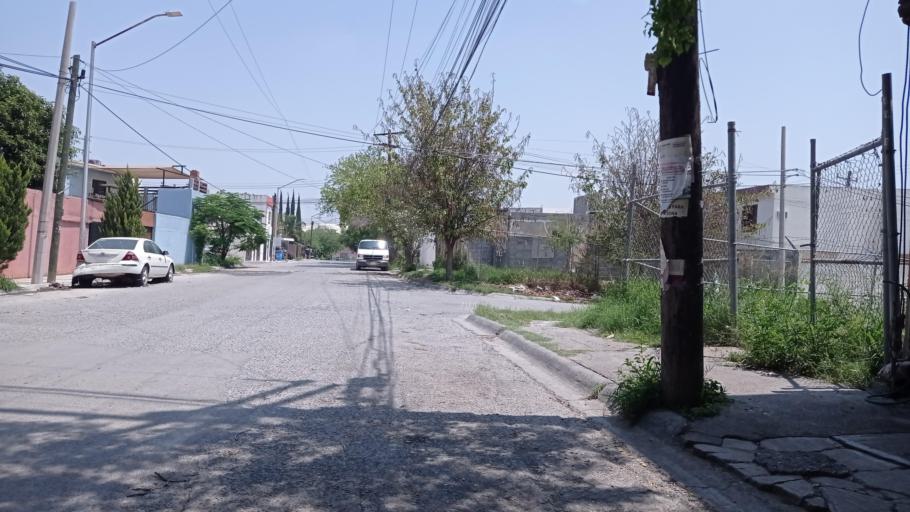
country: MX
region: Nuevo Leon
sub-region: Juarez
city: Jardines de la Silla (Jardines)
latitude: 25.6538
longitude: -100.1902
